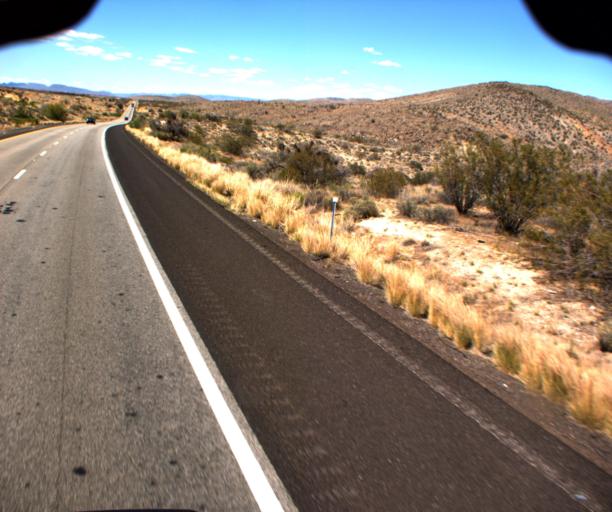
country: US
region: Arizona
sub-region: Mohave County
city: Kingman
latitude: 34.9661
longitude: -113.6702
